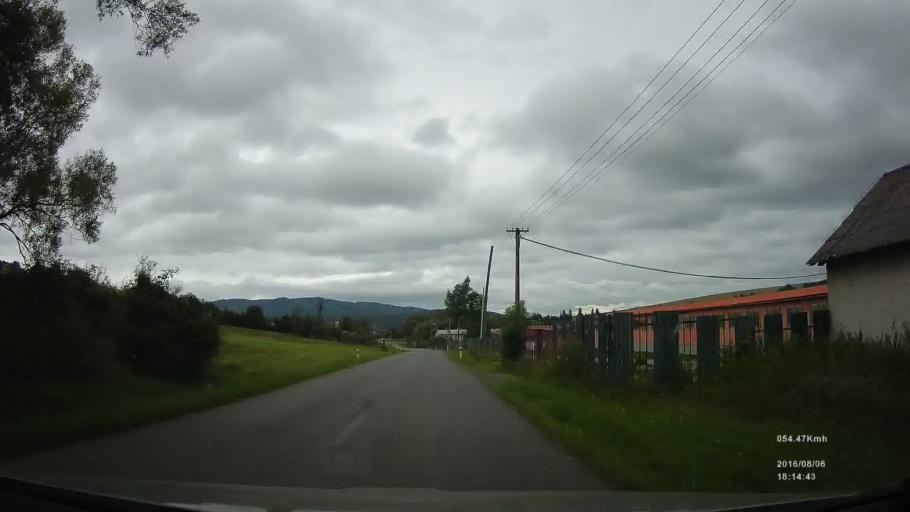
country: SK
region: Presovsky
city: Svidnik
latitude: 49.3509
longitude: 21.5950
